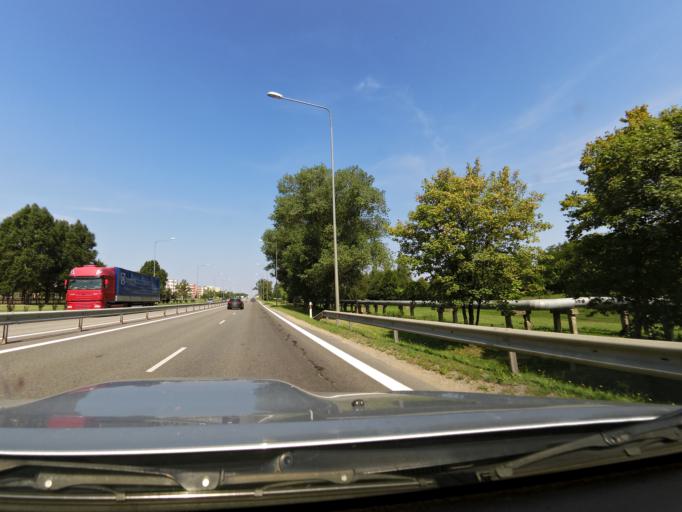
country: LT
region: Siauliu apskritis
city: Radviliskis
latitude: 55.8177
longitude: 23.5385
